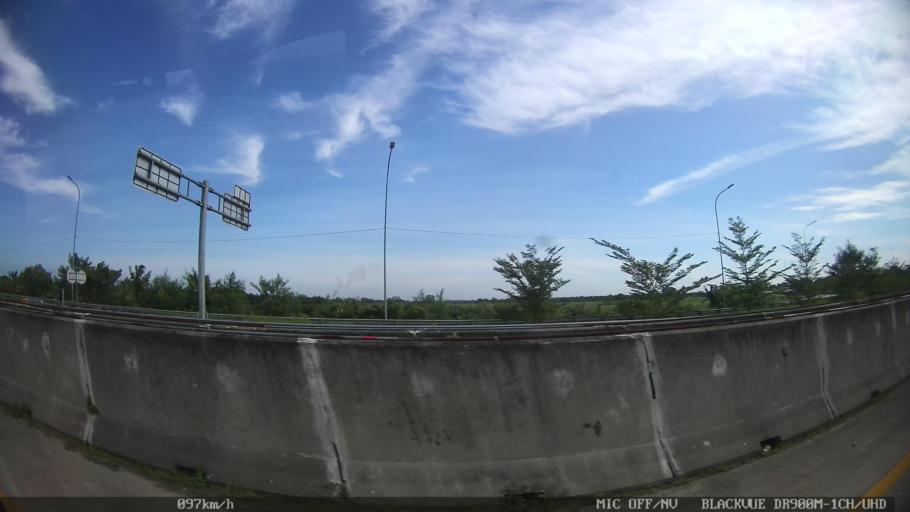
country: ID
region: North Sumatra
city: Sunggal
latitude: 3.6375
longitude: 98.5802
